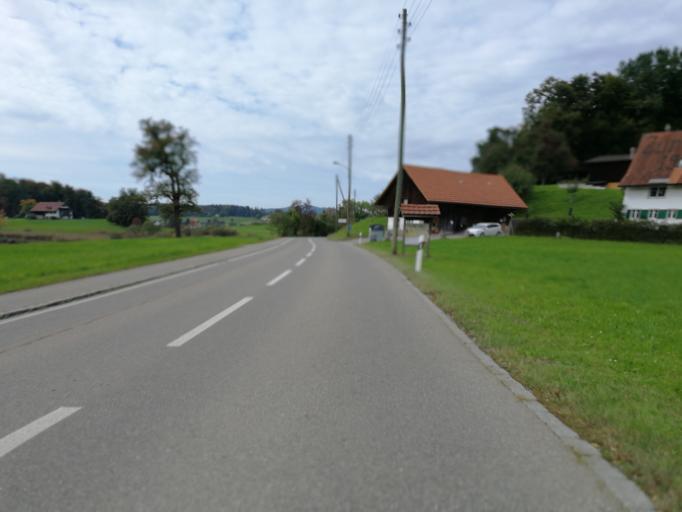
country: CH
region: Zurich
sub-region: Bezirk Meilen
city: Dorf
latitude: 47.2570
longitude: 8.7490
